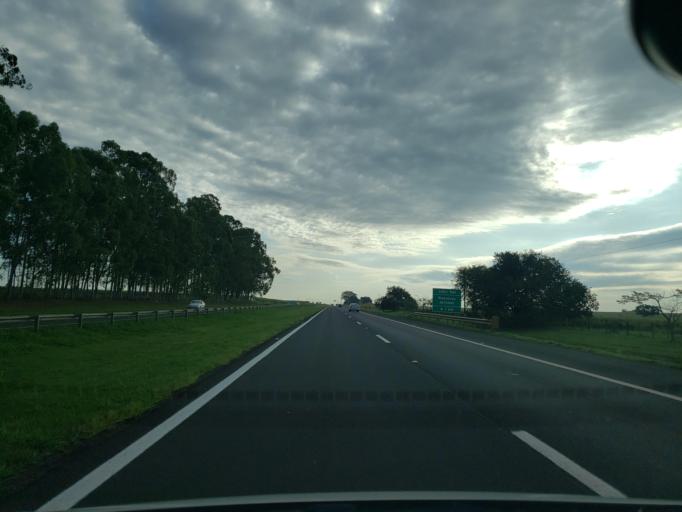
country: BR
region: Sao Paulo
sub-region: Guararapes
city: Guararapes
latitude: -21.2137
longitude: -50.7031
